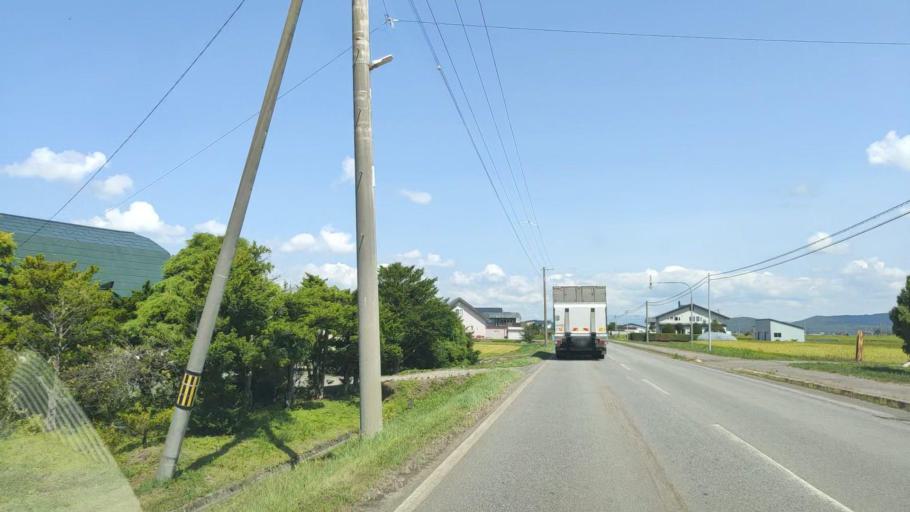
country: JP
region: Hokkaido
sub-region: Asahikawa-shi
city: Asahikawa
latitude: 43.7184
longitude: 142.4576
